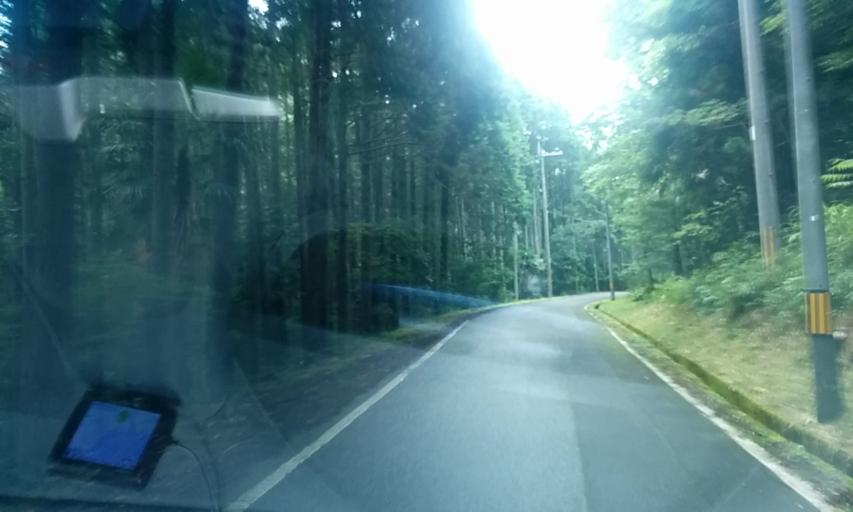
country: JP
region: Kyoto
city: Ayabe
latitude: 35.1870
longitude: 135.2174
